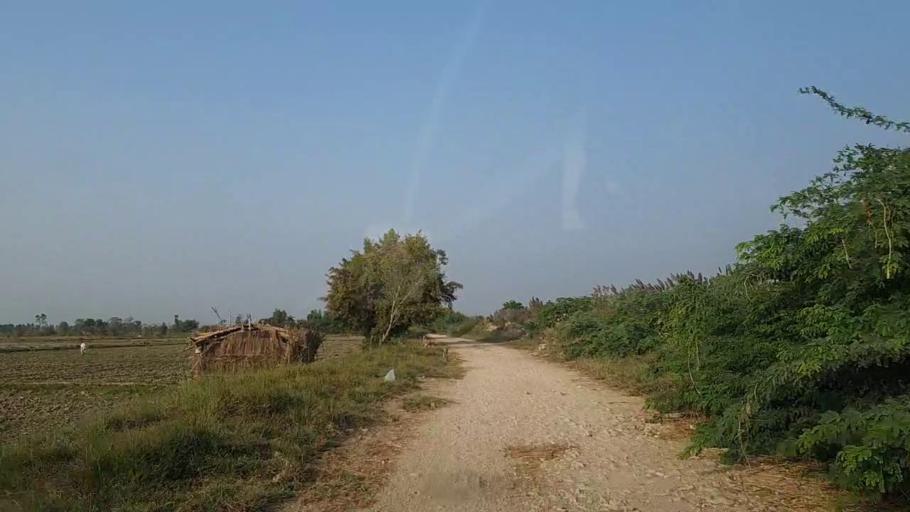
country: PK
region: Sindh
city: Thatta
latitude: 24.6698
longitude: 67.7819
